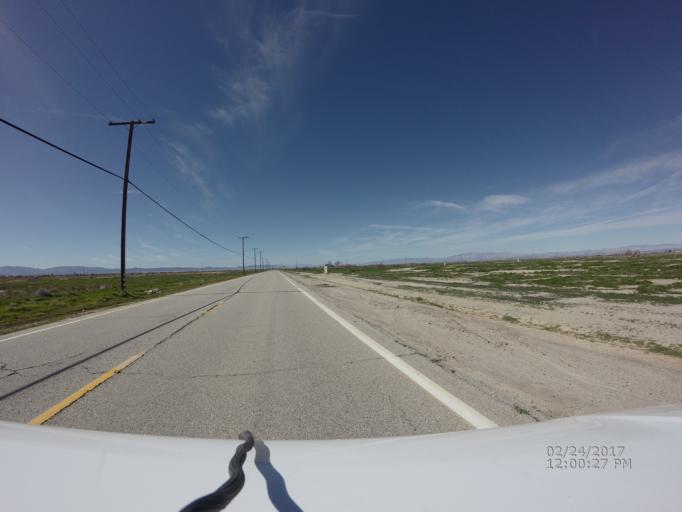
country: US
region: California
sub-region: Los Angeles County
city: Lancaster
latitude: 34.7192
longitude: -118.0196
